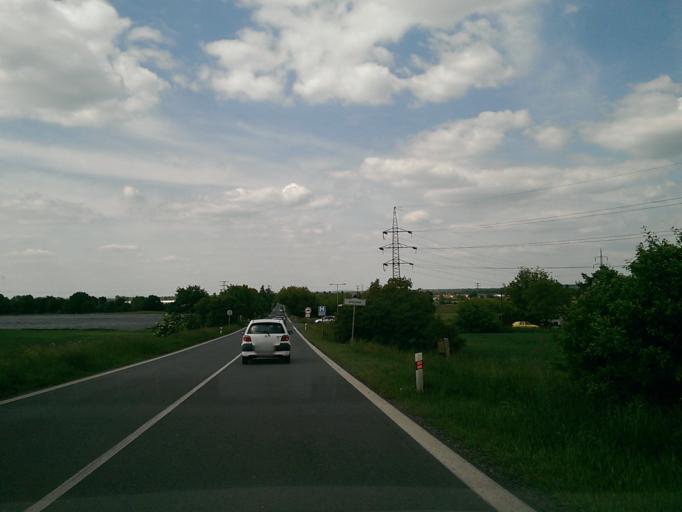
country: CZ
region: Central Bohemia
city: Libis
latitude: 50.2630
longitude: 14.4960
